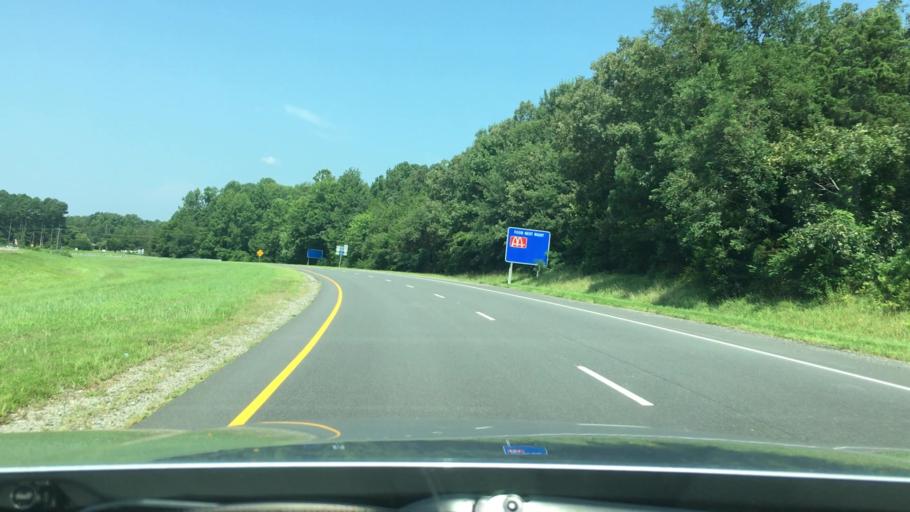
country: US
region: Virginia
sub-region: Caroline County
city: Bowling Green
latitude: 38.0396
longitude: -77.3577
